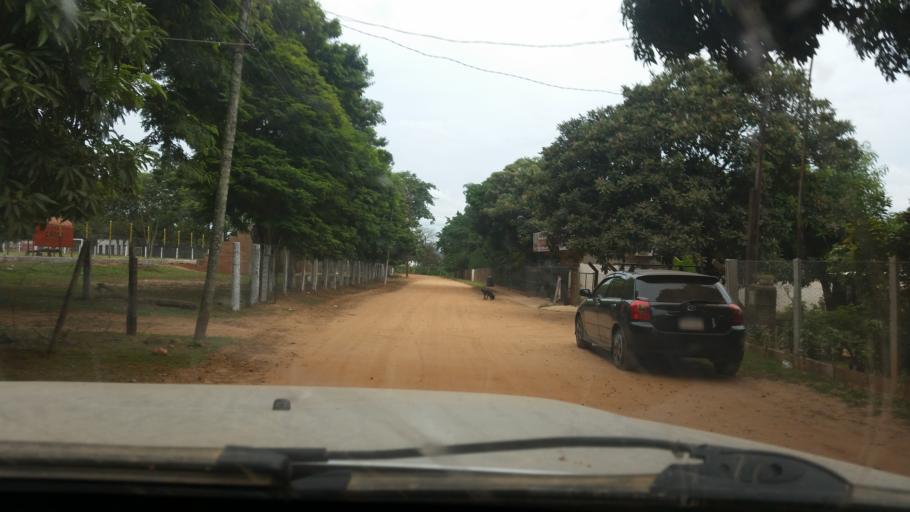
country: PY
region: Guaira
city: Independencia
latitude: -25.7087
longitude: -56.1906
